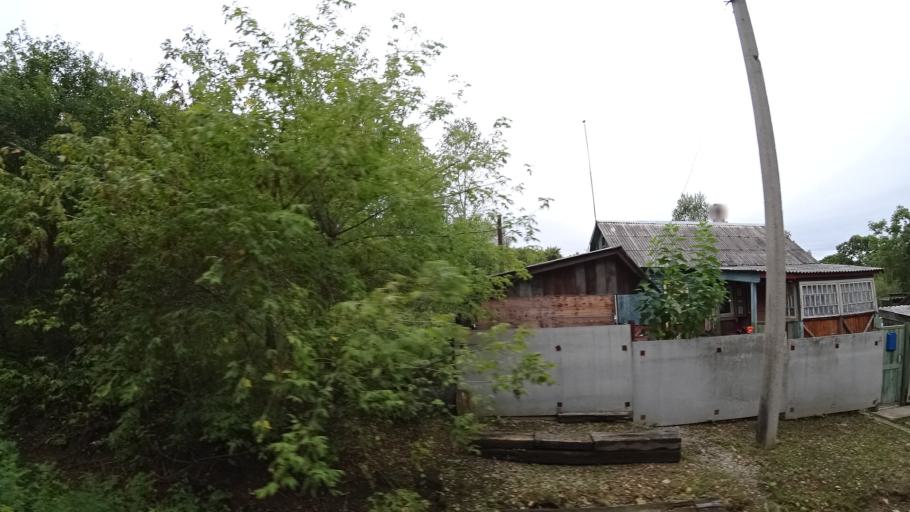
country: RU
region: Primorskiy
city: Rettikhovka
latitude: 44.1603
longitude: 132.7433
